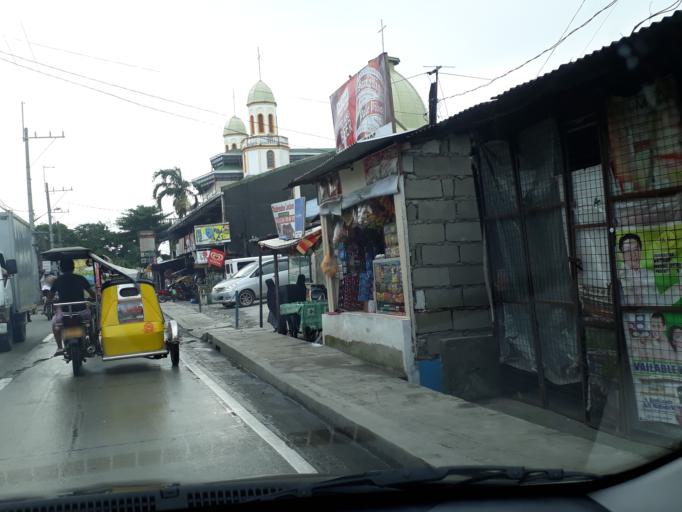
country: PH
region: Calabarzon
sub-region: Province of Rizal
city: Valenzuela
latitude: 14.7094
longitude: 120.9608
